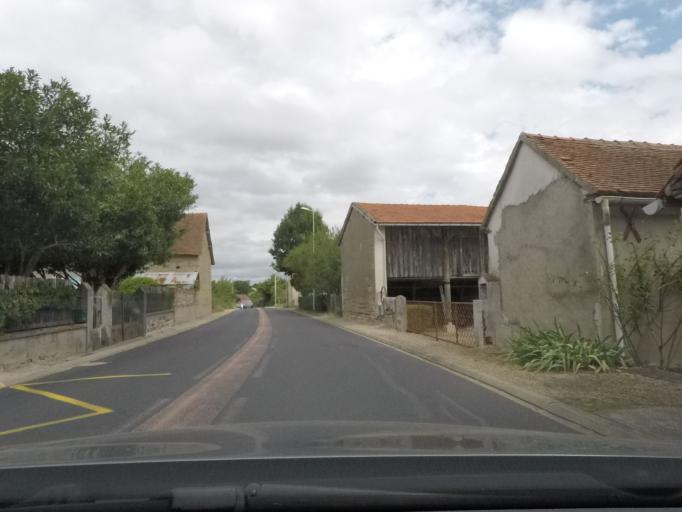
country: FR
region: Auvergne
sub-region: Departement du Puy-de-Dome
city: Randan
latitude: 46.0426
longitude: 3.3615
